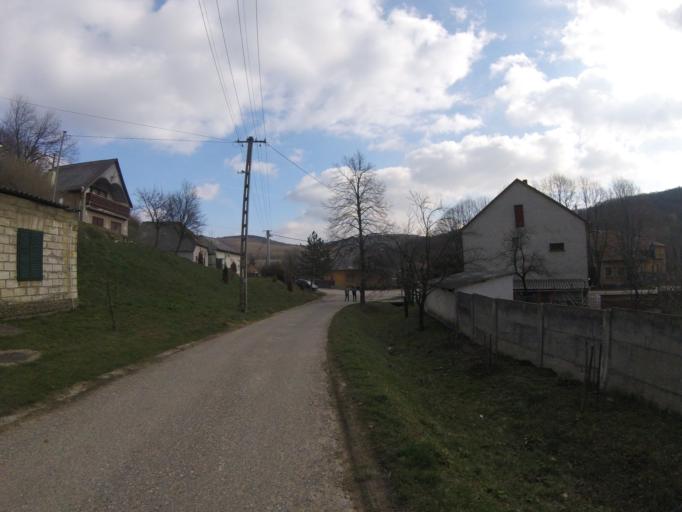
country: HU
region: Komarom-Esztergom
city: Tat
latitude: 47.7290
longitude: 18.5981
